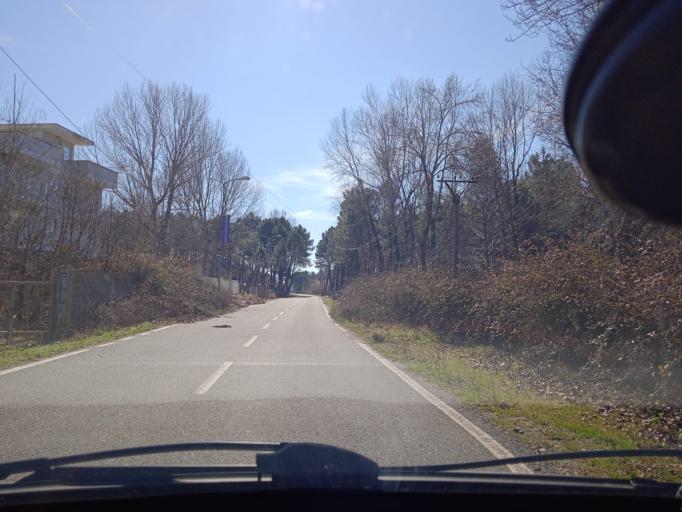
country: AL
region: Shkoder
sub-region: Rrethi i Shkodres
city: Velipoje
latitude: 41.8653
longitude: 19.4062
